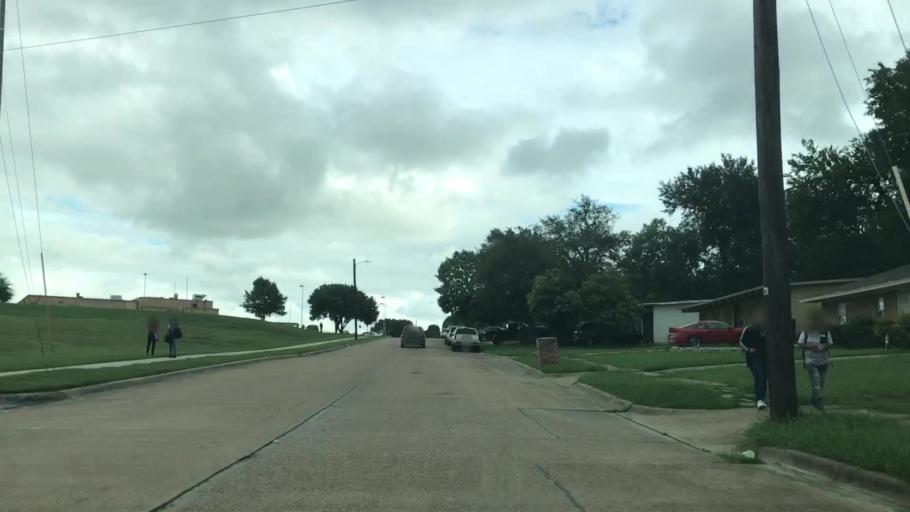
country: US
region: Texas
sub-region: Dallas County
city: Garland
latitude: 32.8976
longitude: -96.6182
